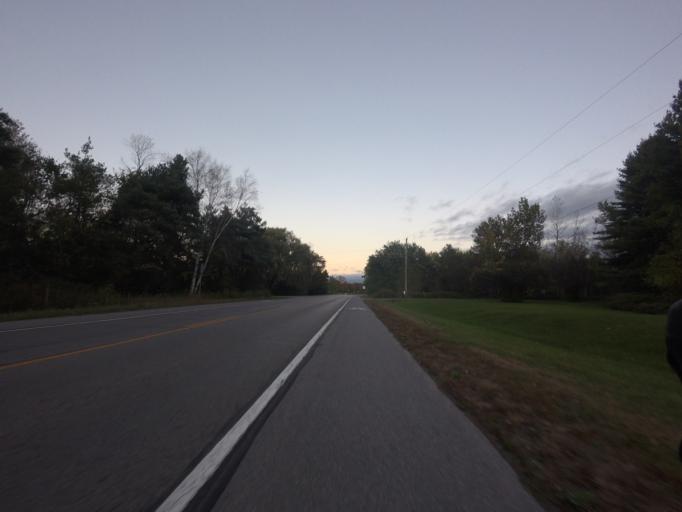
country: CA
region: Ontario
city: Quinte West
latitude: 44.0408
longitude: -77.6773
